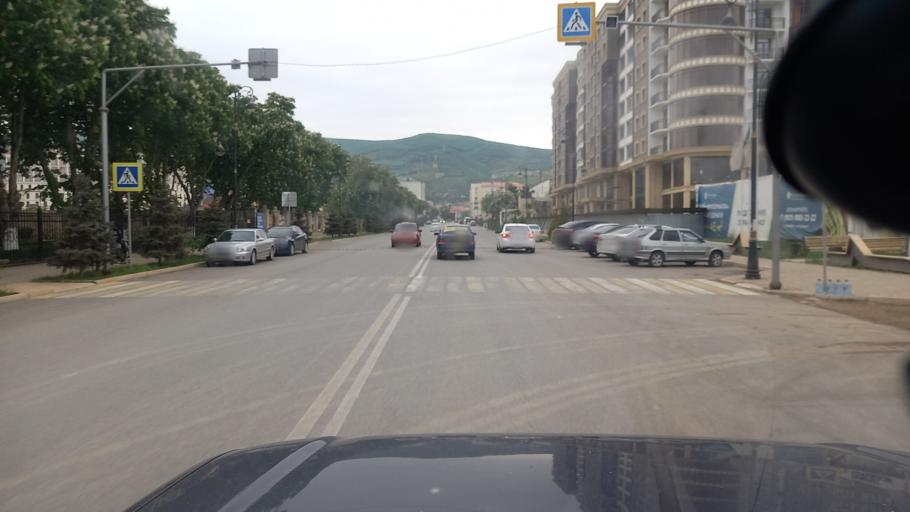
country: RU
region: Dagestan
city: Derbent
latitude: 42.0634
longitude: 48.2939
